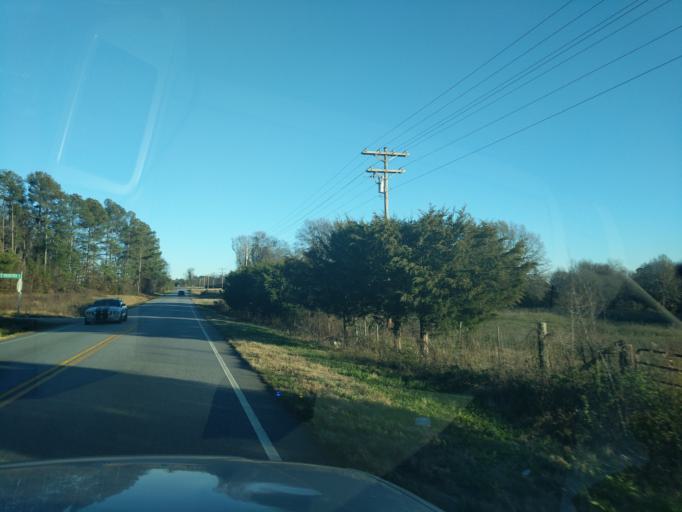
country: US
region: South Carolina
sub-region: Oconee County
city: Seneca
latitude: 34.5943
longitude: -82.9977
